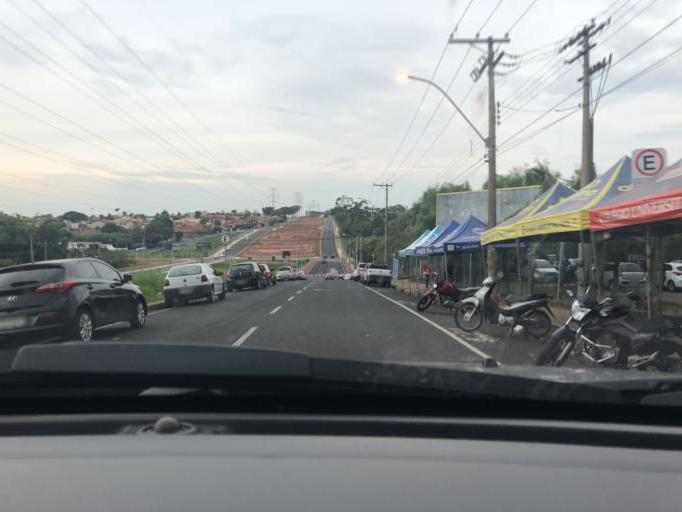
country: BR
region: Sao Paulo
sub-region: Sao Jose Do Rio Preto
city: Sao Jose do Rio Preto
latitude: -20.8426
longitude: -49.4127
